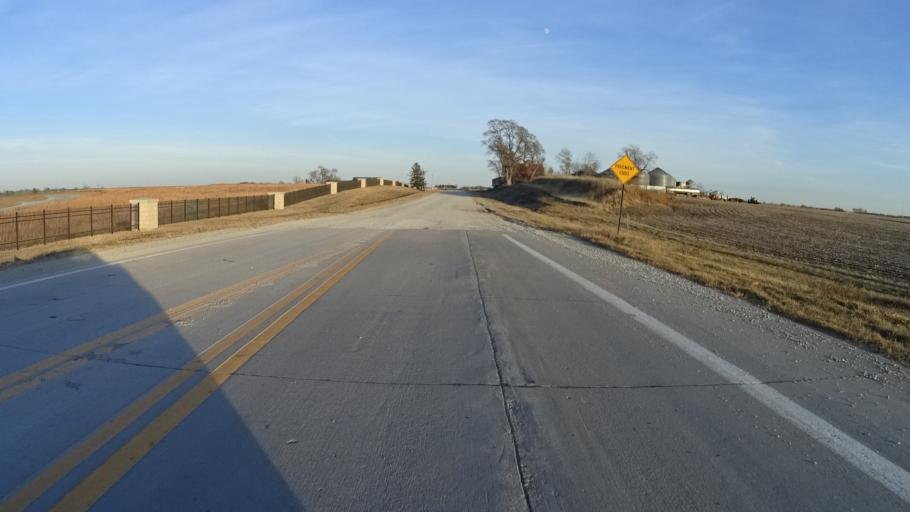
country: US
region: Nebraska
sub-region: Sarpy County
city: Springfield
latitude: 41.1325
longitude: -96.1341
